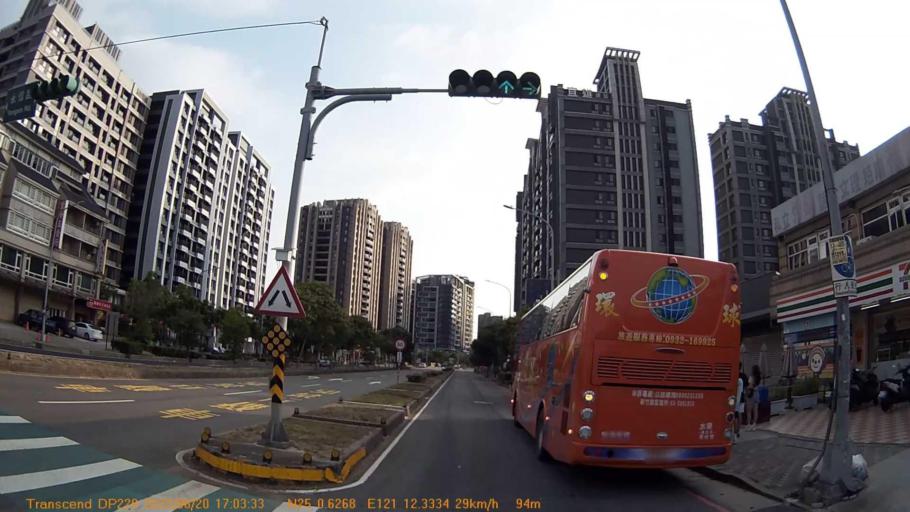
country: TW
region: Taiwan
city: Taoyuan City
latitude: 25.0102
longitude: 121.2053
